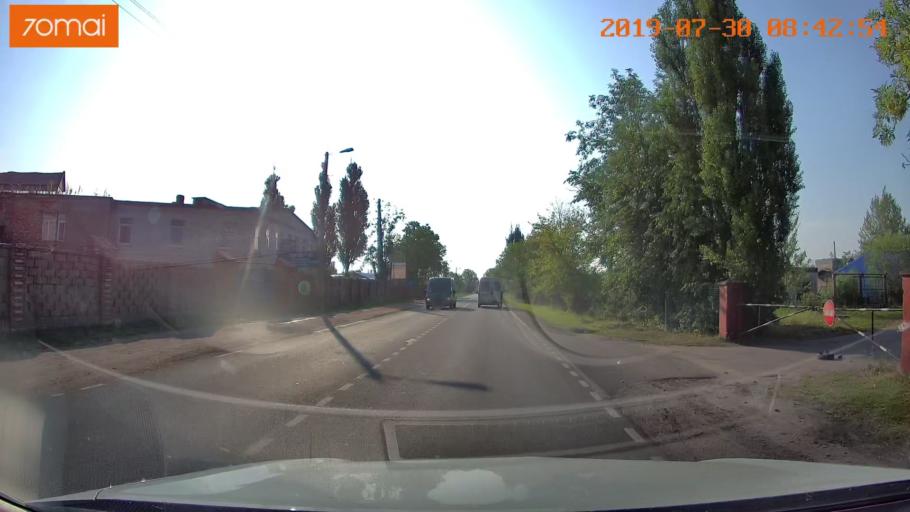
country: RU
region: Kaliningrad
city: Chernyakhovsk
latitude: 54.6283
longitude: 21.8339
